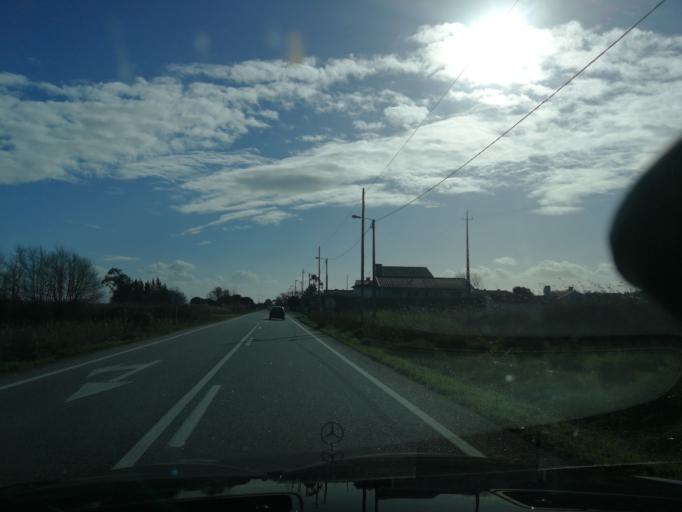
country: PT
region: Aveiro
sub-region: Estarreja
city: Pardilho
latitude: 40.8174
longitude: -8.6700
